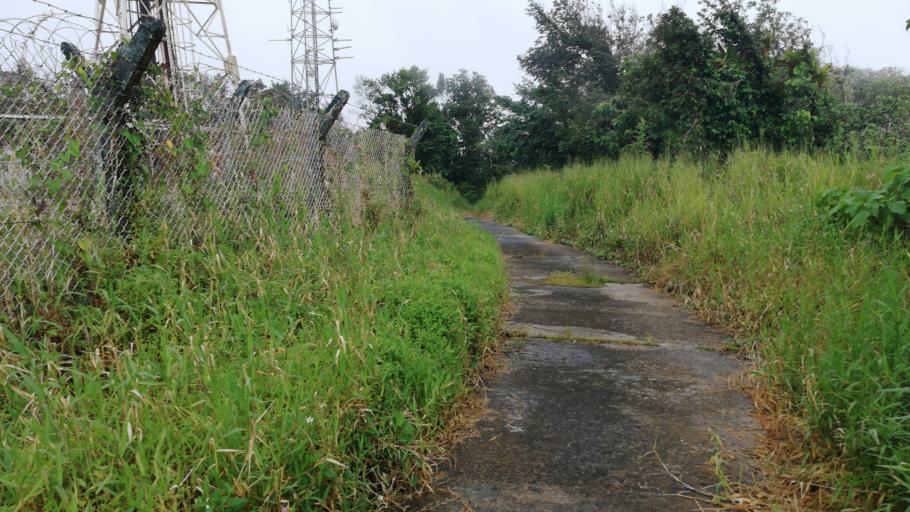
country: GP
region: Guadeloupe
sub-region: Guadeloupe
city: Pointe-Noire
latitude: 16.1860
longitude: -61.7493
